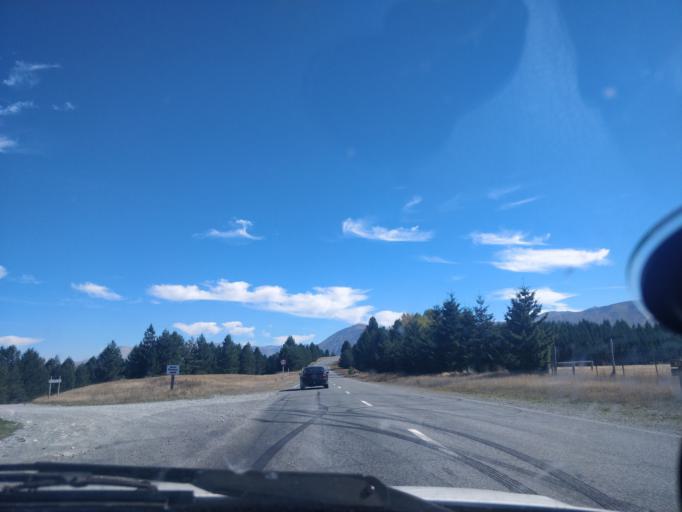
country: NZ
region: Otago
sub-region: Queenstown-Lakes District
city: Wanaka
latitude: -44.2722
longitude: 170.0523
